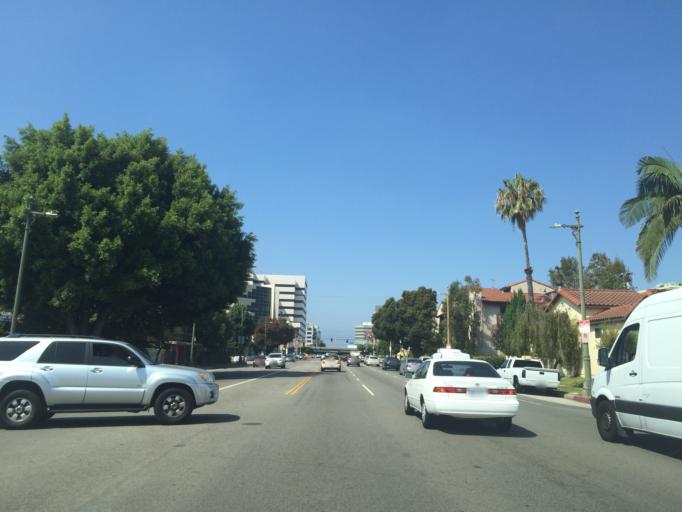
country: US
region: California
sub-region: Los Angeles County
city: Westwood, Los Angeles
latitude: 34.0413
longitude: -118.4361
